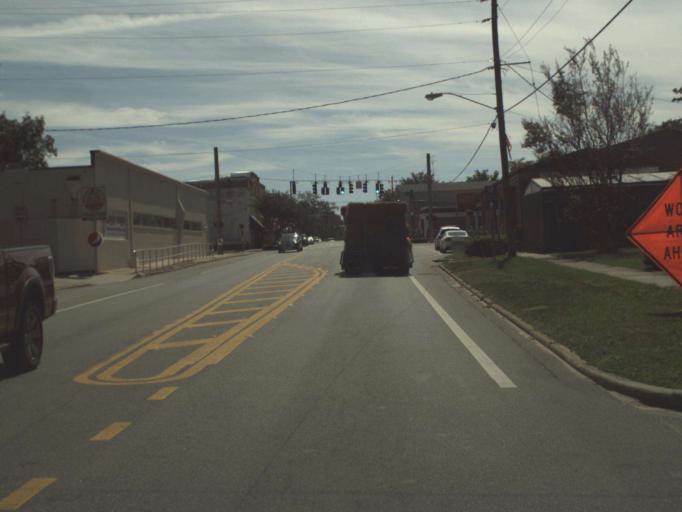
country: US
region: Florida
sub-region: Washington County
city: Chipley
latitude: 30.7827
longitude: -85.5388
